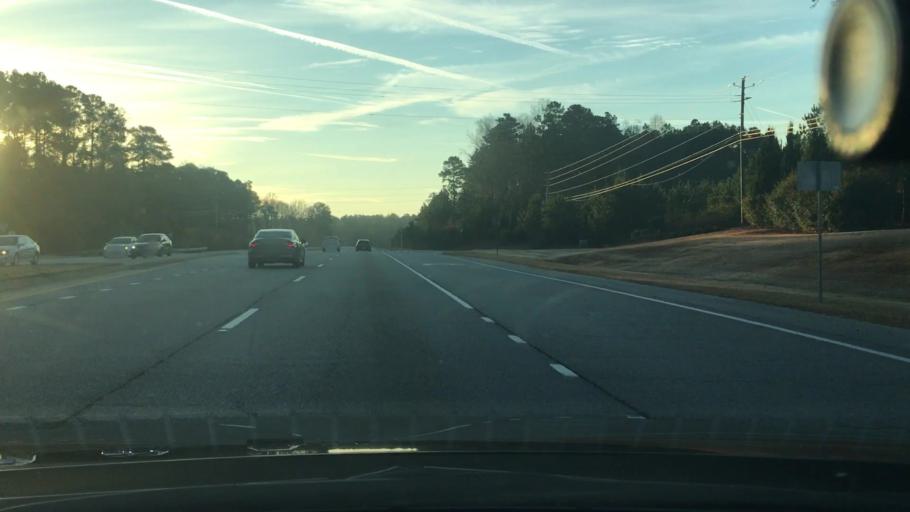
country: US
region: Georgia
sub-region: Fayette County
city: Peachtree City
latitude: 33.3680
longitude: -84.5662
